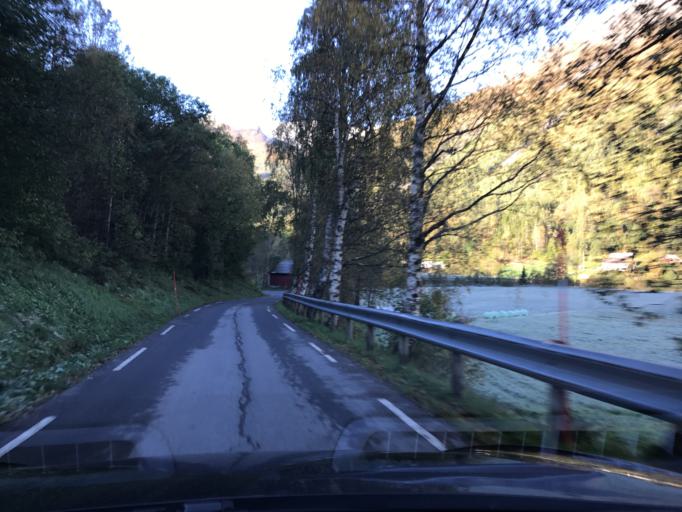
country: NO
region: More og Romsdal
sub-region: Norddal
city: Valldal
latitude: 62.3145
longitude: 7.2962
